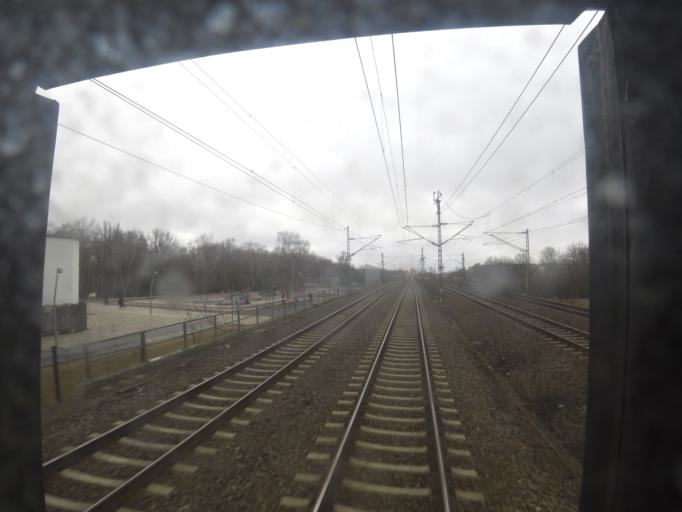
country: DE
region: Berlin
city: Tiergarten Bezirk
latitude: 52.4960
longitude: 13.3729
